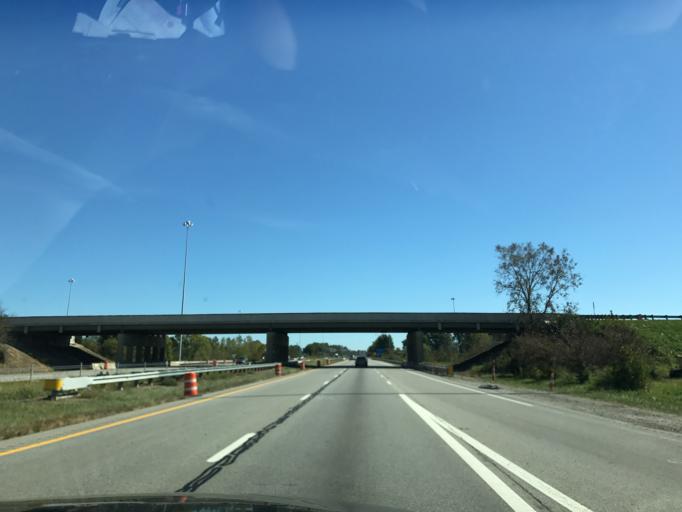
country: US
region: Ohio
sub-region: Licking County
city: Buckeye Lake
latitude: 39.9450
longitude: -82.4819
